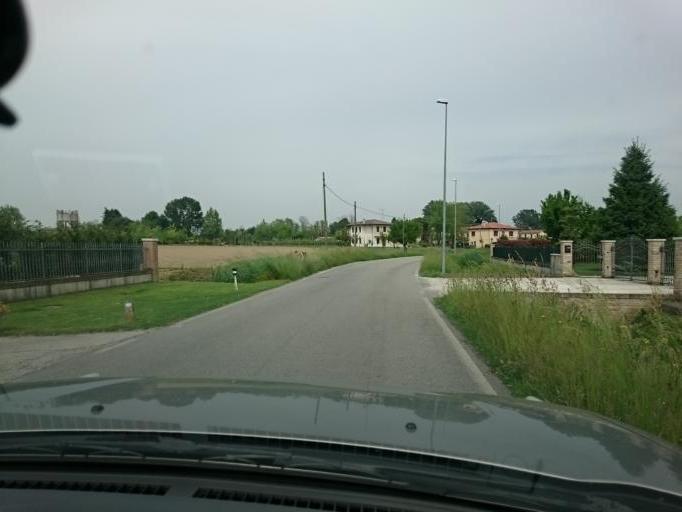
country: IT
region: Veneto
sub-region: Provincia di Venezia
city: Stra
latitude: 45.4131
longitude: 12.0234
